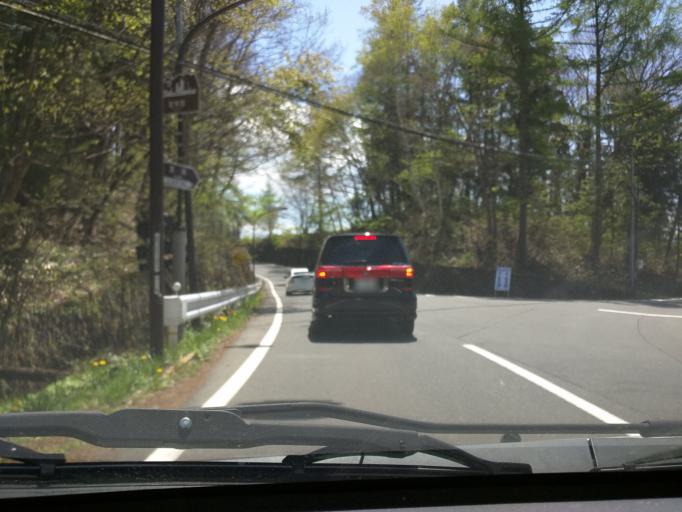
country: JP
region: Nagano
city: Nagano-shi
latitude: 36.7261
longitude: 138.0803
